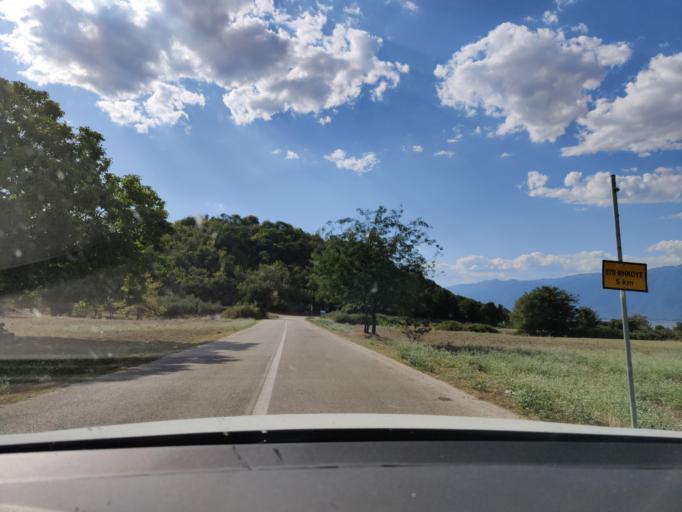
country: GR
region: Central Macedonia
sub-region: Nomos Serron
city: Chrysochorafa
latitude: 41.1622
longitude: 23.1852
